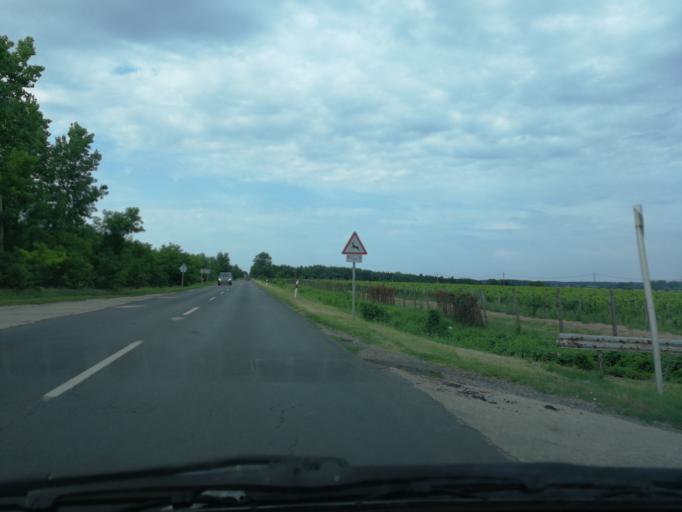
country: HU
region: Bacs-Kiskun
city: Ersekcsanad
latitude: 46.2344
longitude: 18.9748
